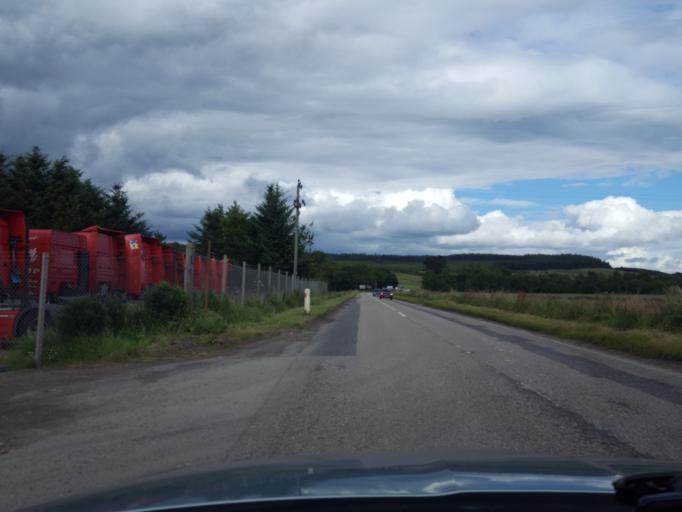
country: GB
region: Scotland
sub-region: Moray
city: Rothes
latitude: 57.4268
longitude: -3.3474
